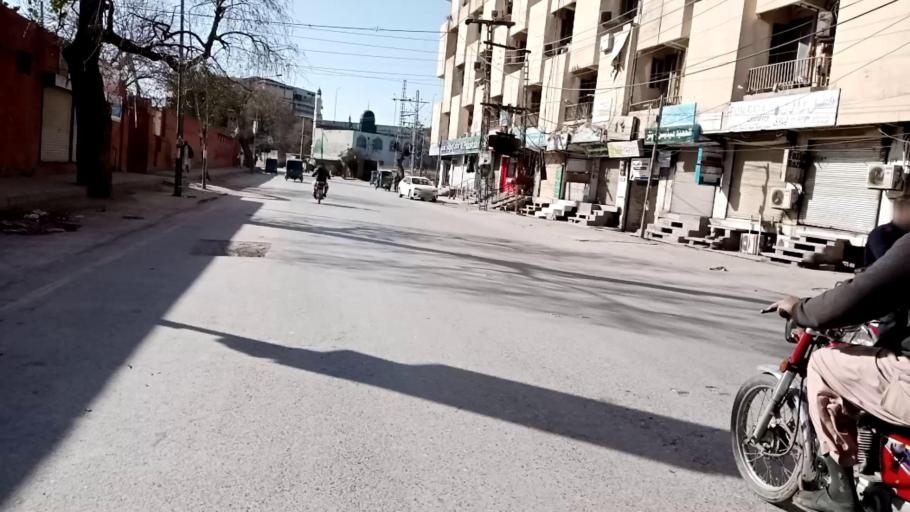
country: PK
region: Khyber Pakhtunkhwa
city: Peshawar
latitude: 34.0038
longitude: 71.5579
